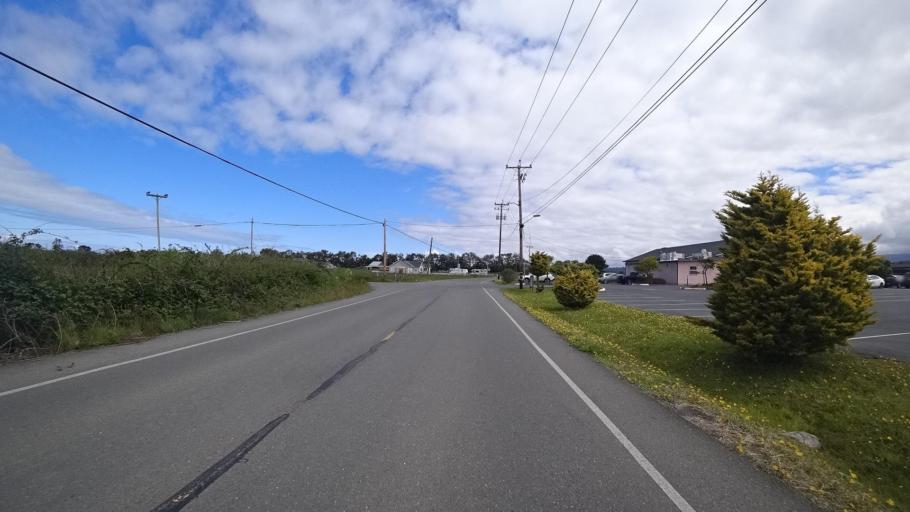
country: US
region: California
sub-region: Humboldt County
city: Arcata
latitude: 40.8790
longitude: -124.1011
